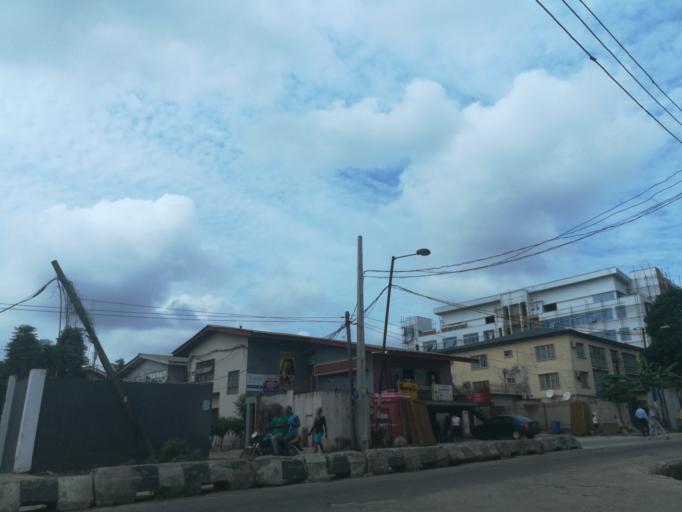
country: NG
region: Lagos
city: Somolu
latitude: 6.5571
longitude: 3.3649
